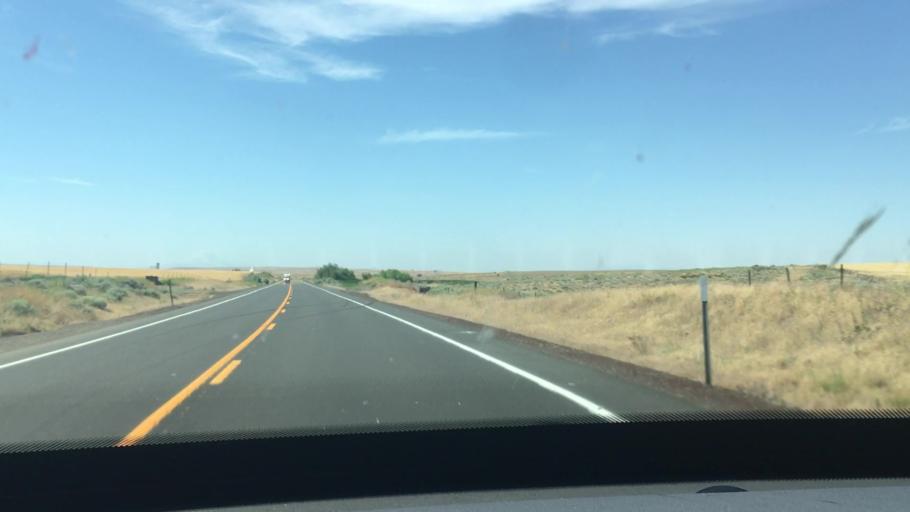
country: US
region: Oregon
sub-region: Sherman County
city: Moro
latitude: 45.3323
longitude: -120.7693
